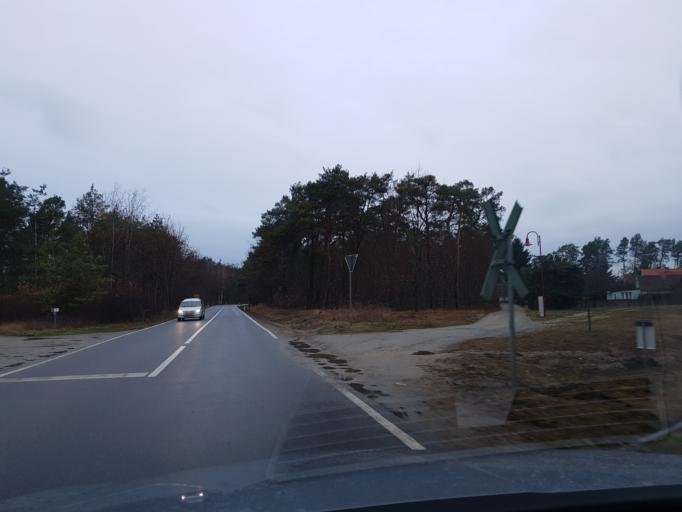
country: DE
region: Brandenburg
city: Finsterwalde
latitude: 51.6490
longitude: 13.6958
